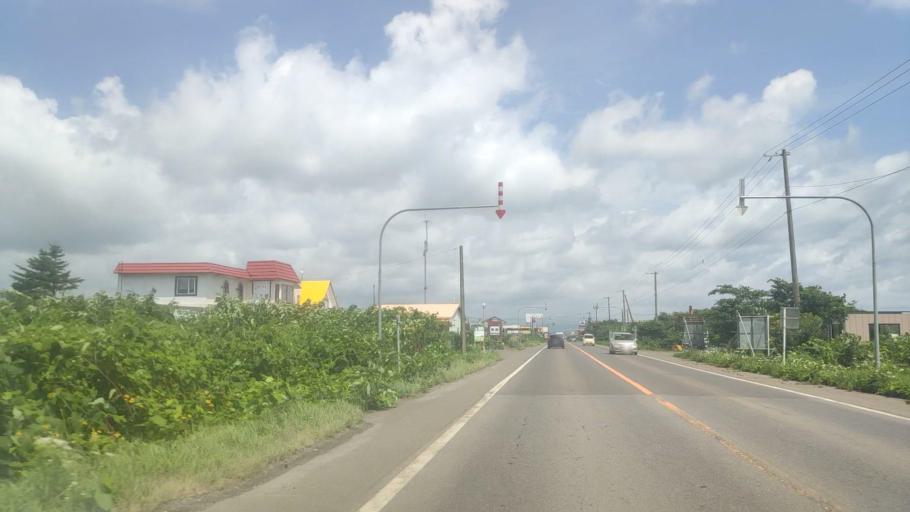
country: JP
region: Hokkaido
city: Niseko Town
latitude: 42.4893
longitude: 140.3570
